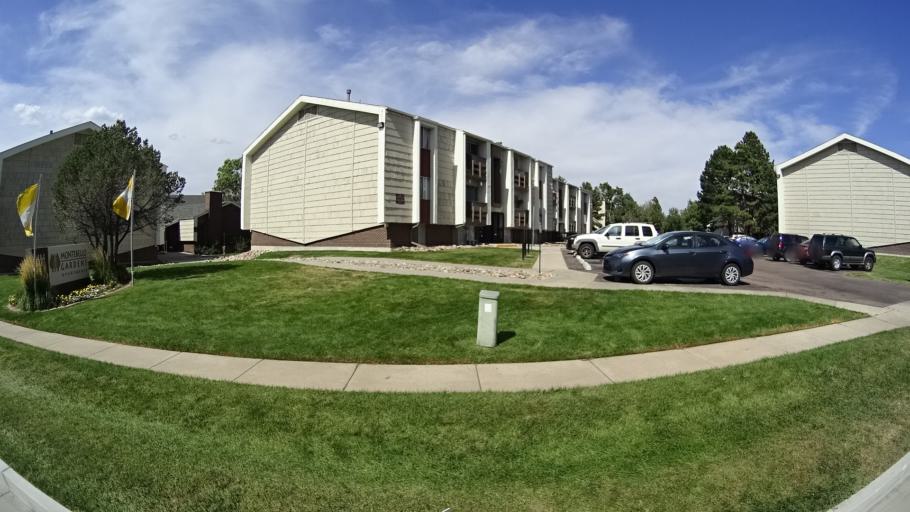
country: US
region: Colorado
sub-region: El Paso County
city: Cimarron Hills
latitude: 38.8958
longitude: -104.7539
